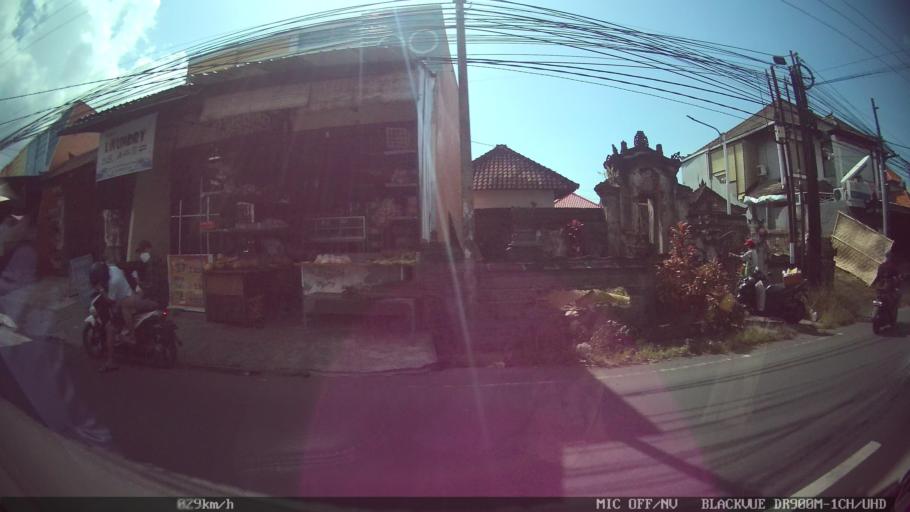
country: ID
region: Bali
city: Karyadharma
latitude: -8.7139
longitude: 115.2001
